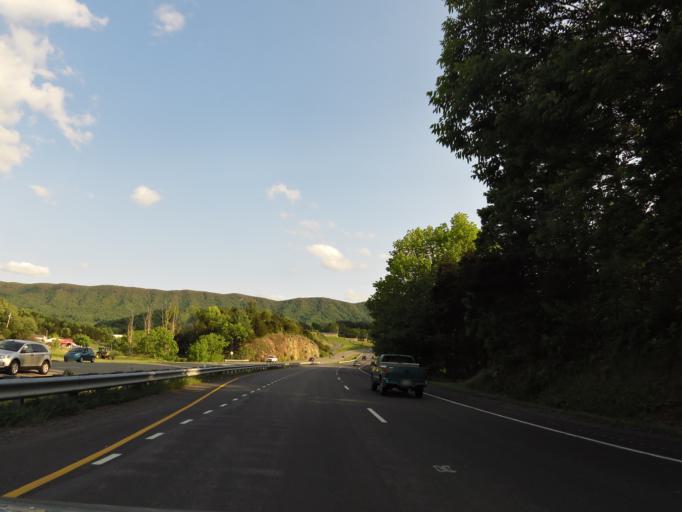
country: US
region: Virginia
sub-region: Tazewell County
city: Claypool Hill
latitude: 37.0147
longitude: -81.7953
